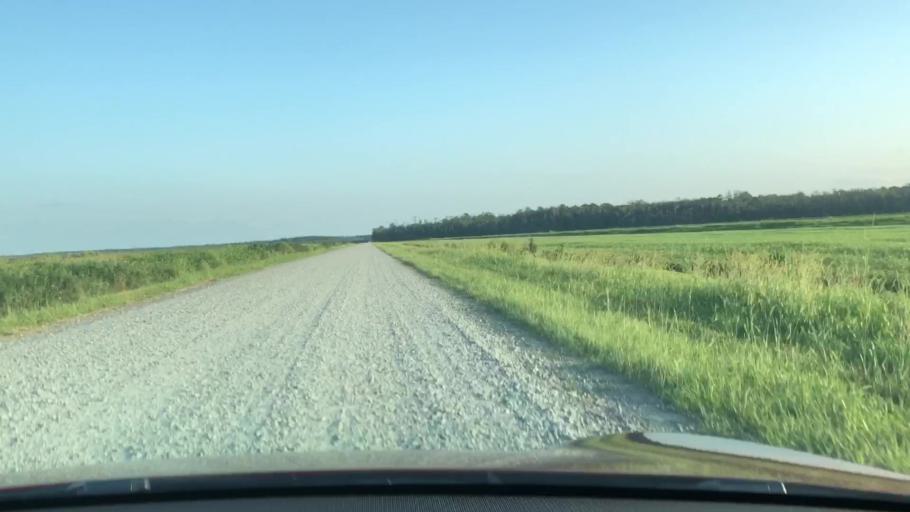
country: US
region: North Carolina
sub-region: Dare County
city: Manteo
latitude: 35.8522
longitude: -75.8619
